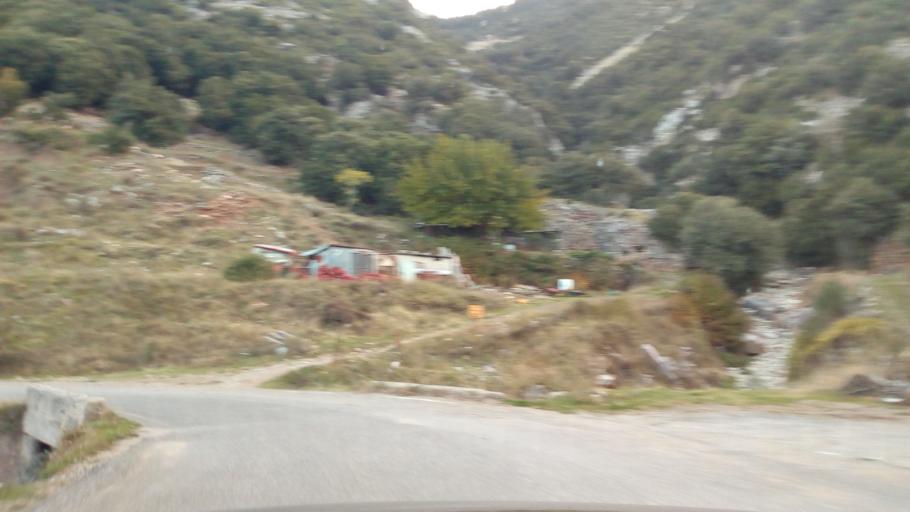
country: GR
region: West Greece
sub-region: Nomos Aitolias kai Akarnanias
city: Nafpaktos
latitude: 38.5203
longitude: 21.8437
